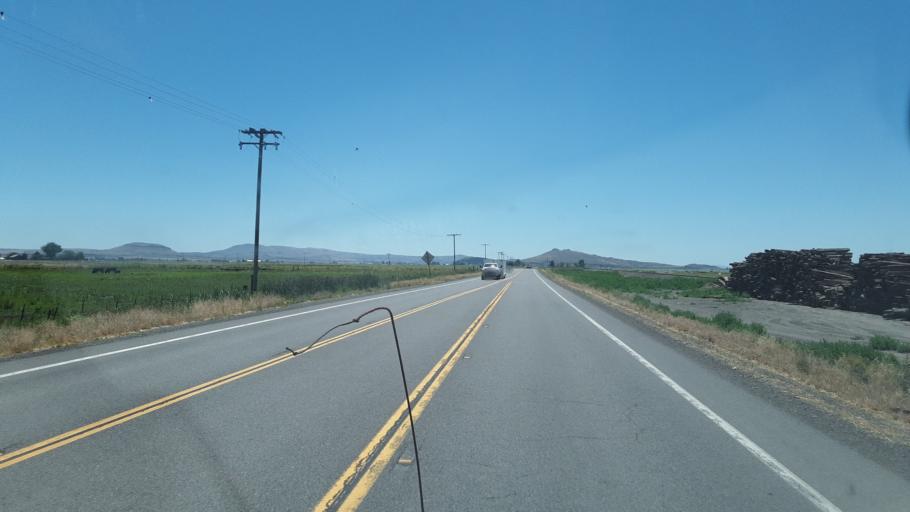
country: US
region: California
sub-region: Siskiyou County
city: Tulelake
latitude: 41.9396
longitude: -121.4551
